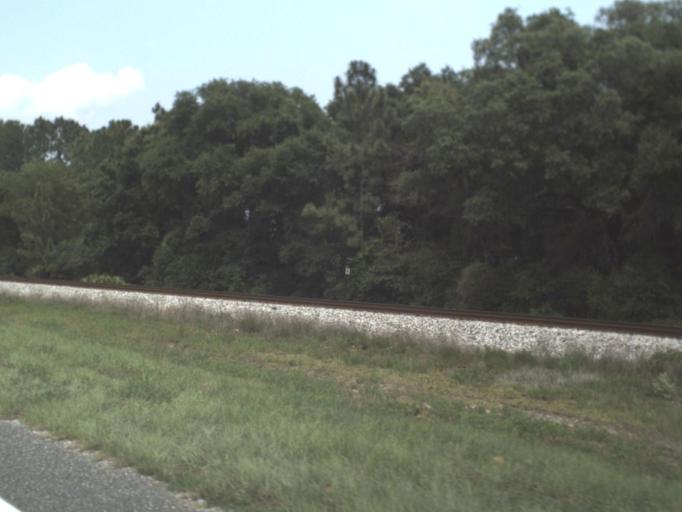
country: US
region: Florida
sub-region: Putnam County
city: Palatka
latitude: 29.7415
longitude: -81.6435
